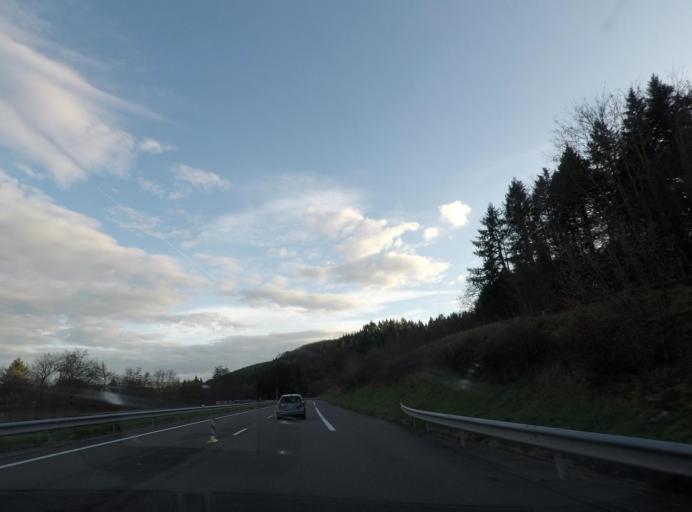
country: FR
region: Bourgogne
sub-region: Departement de Saone-et-Loire
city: Matour
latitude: 46.3781
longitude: 4.5290
